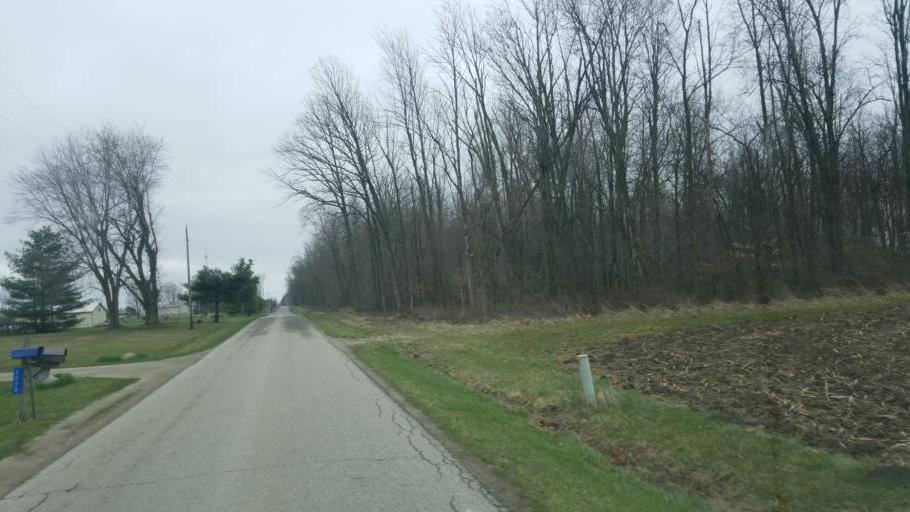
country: US
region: Ohio
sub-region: Crawford County
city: Bucyrus
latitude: 40.8559
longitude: -82.9643
